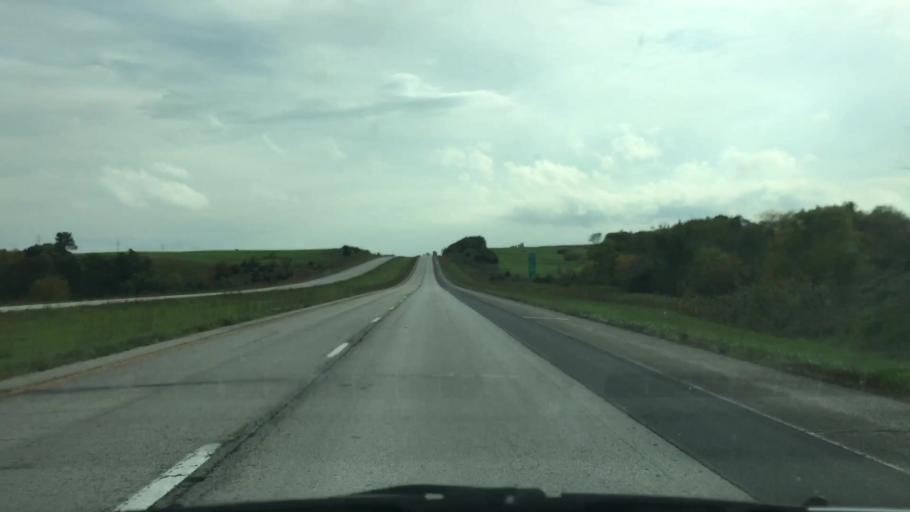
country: US
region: Iowa
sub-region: Decatur County
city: Lamoni
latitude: 40.5052
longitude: -93.9663
